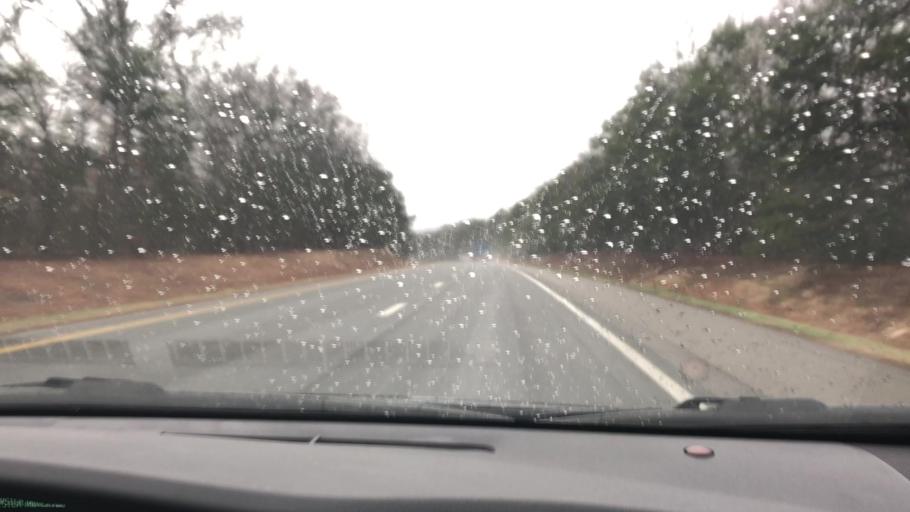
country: US
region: Virginia
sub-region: Fluvanna County
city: Lake Monticello
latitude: 37.9927
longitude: -78.2494
